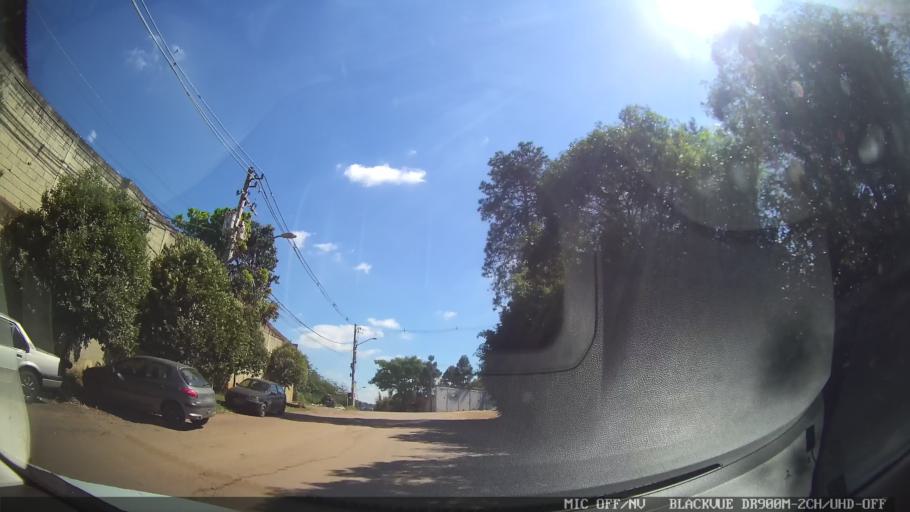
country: BR
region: Sao Paulo
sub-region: Cajamar
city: Cajamar
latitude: -23.4139
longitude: -46.8134
